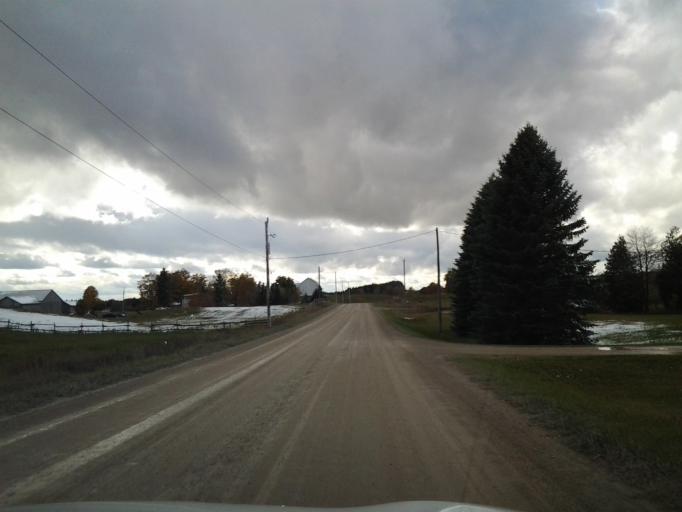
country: CA
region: Ontario
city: Shelburne
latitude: 44.0581
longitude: -80.1102
